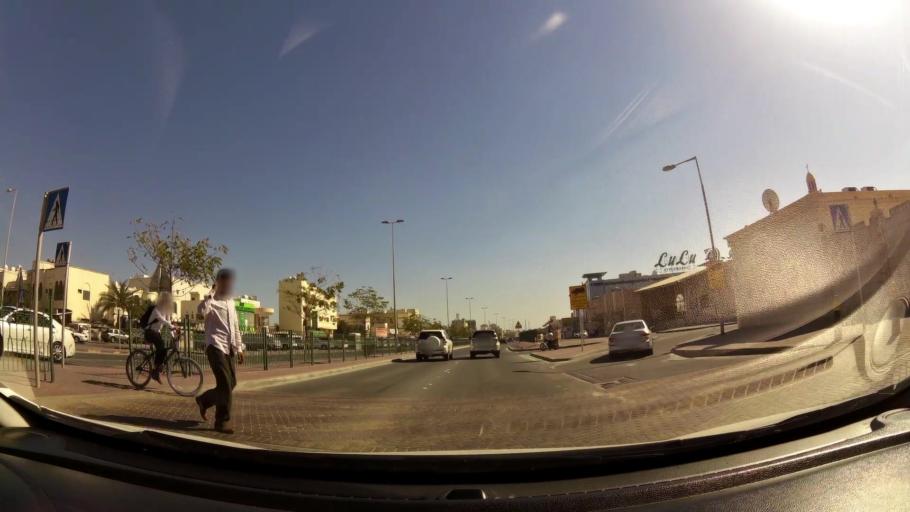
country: BH
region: Muharraq
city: Al Hadd
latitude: 26.2405
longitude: 50.6517
